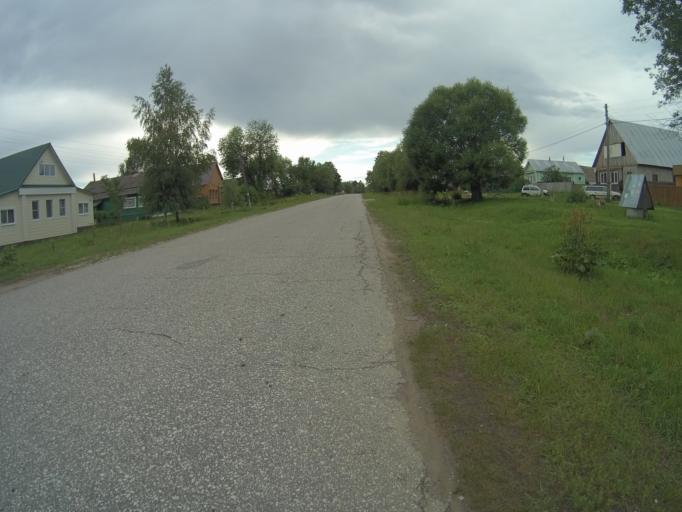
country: RU
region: Vladimir
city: Kameshkovo
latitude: 56.1928
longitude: 40.9209
